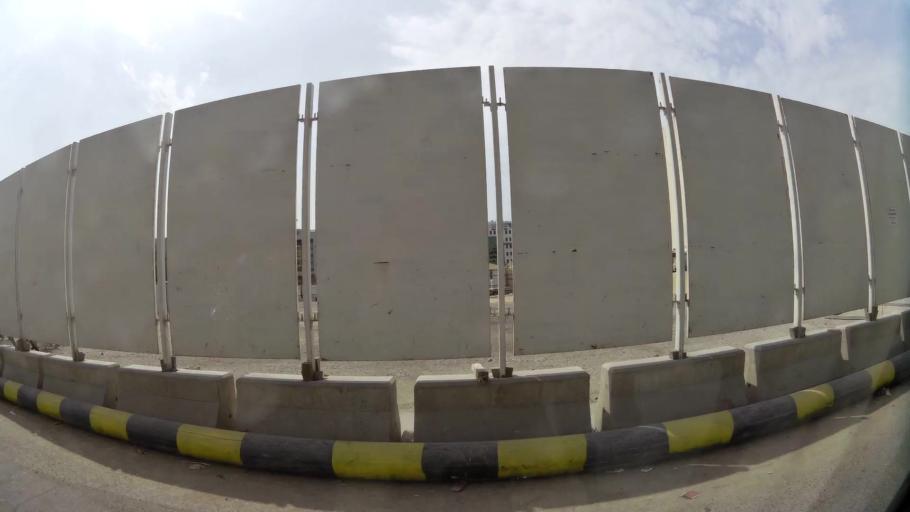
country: QA
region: Baladiyat ad Dawhah
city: Doha
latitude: 25.2838
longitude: 51.5369
